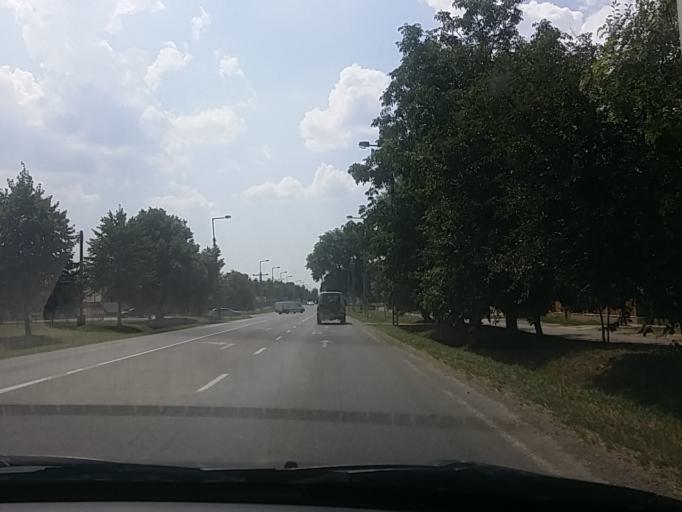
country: HU
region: Tolna
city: Dombovar
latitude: 46.3964
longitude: 18.1480
